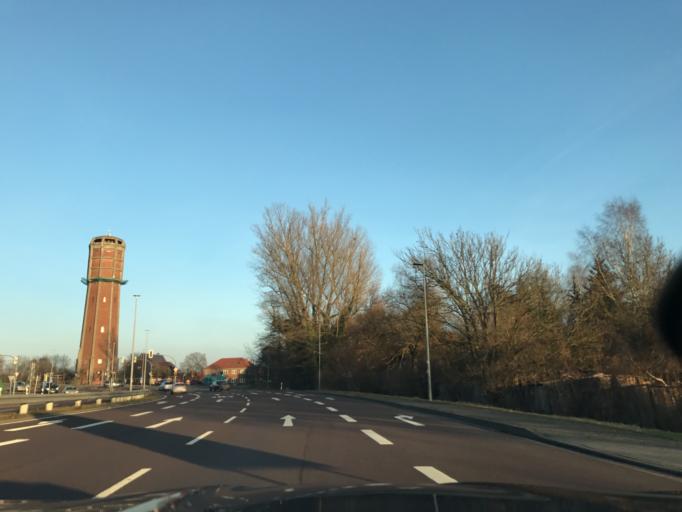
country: DE
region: Saxony-Anhalt
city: Genthin
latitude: 52.4080
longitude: 12.1518
